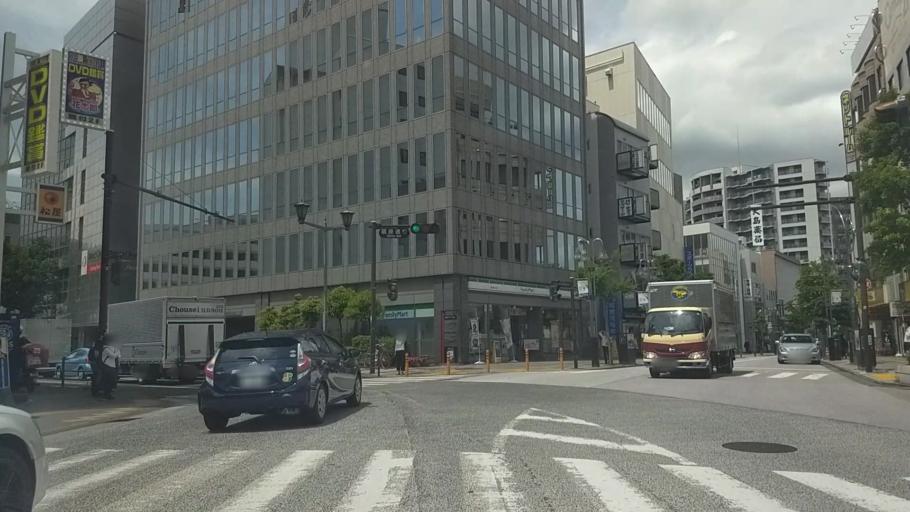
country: JP
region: Kanagawa
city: Fujisawa
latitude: 35.3401
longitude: 139.4864
